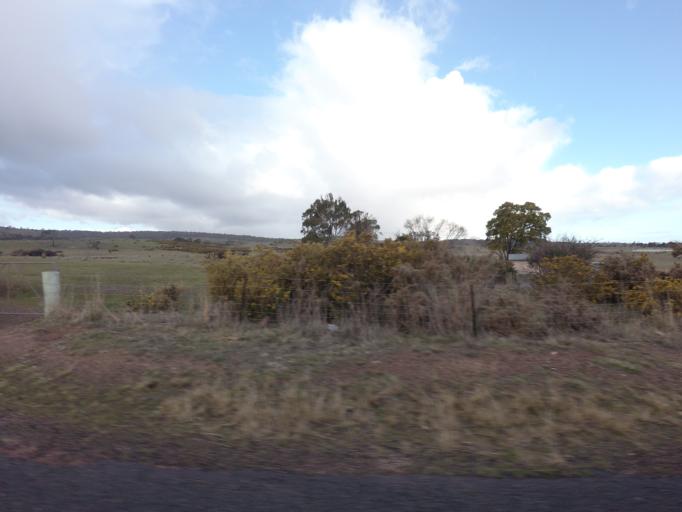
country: AU
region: Tasmania
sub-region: Break O'Day
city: St Helens
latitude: -42.0024
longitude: 148.0858
